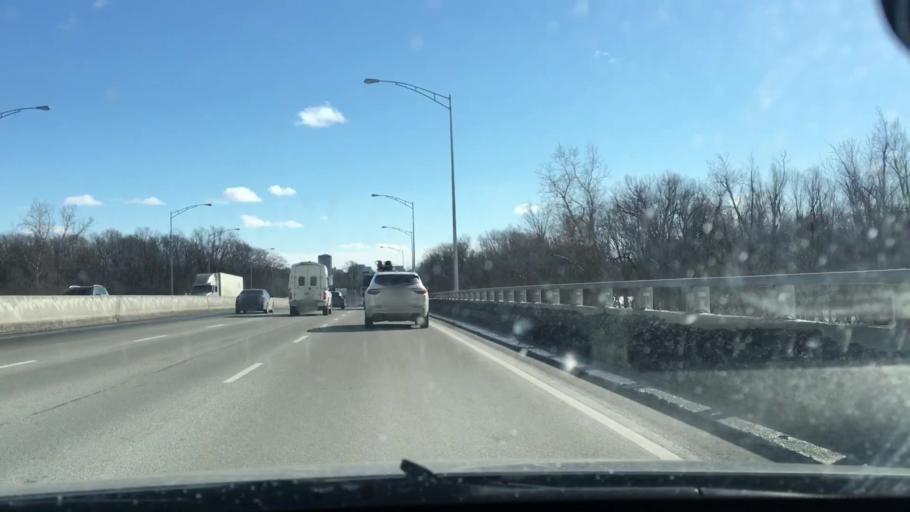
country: CA
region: Quebec
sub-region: Outaouais
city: Gatineau
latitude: 45.4563
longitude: -75.7162
